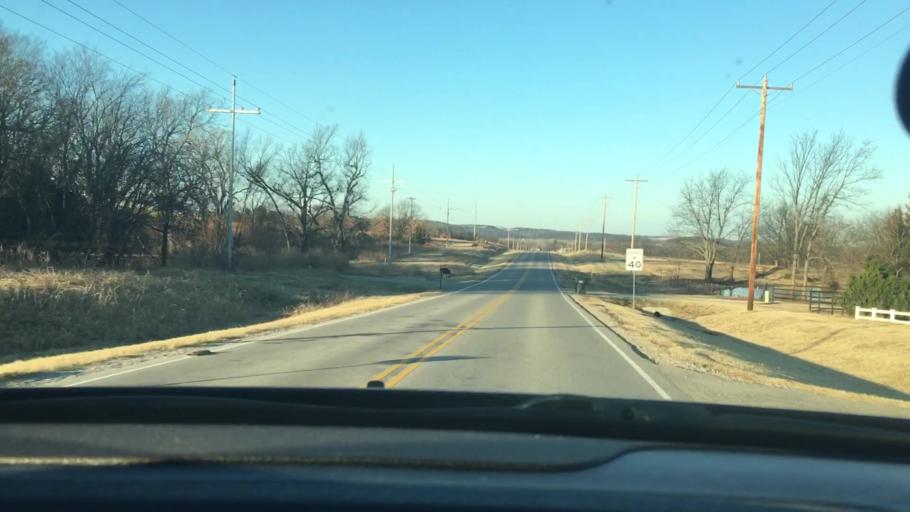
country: US
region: Oklahoma
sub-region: Murray County
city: Davis
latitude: 34.4774
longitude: -97.1169
